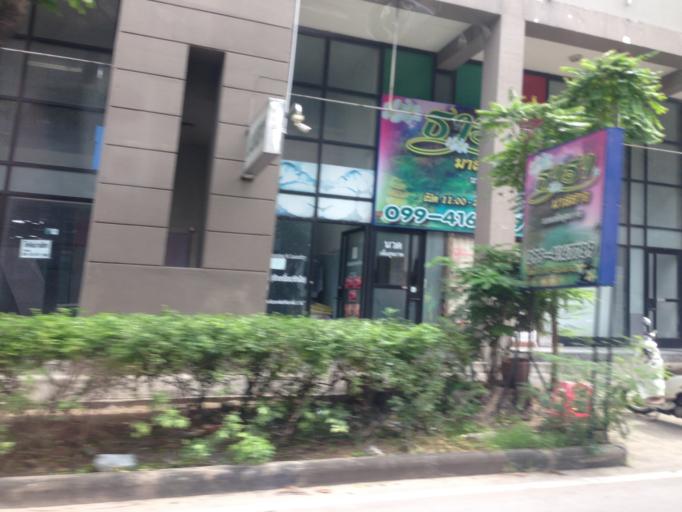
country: TH
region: Nonthaburi
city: Pak Kret
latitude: 13.9224
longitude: 100.5375
